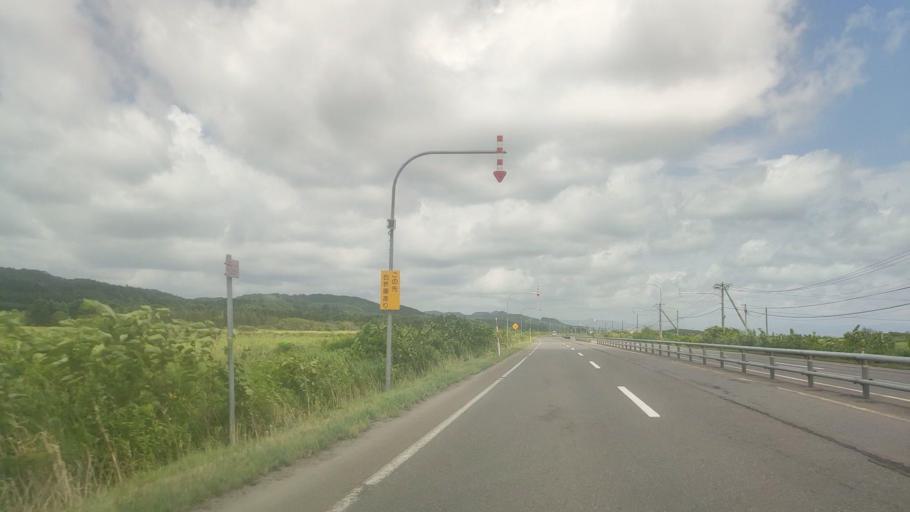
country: JP
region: Hokkaido
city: Niseko Town
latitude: 42.4072
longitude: 140.3056
